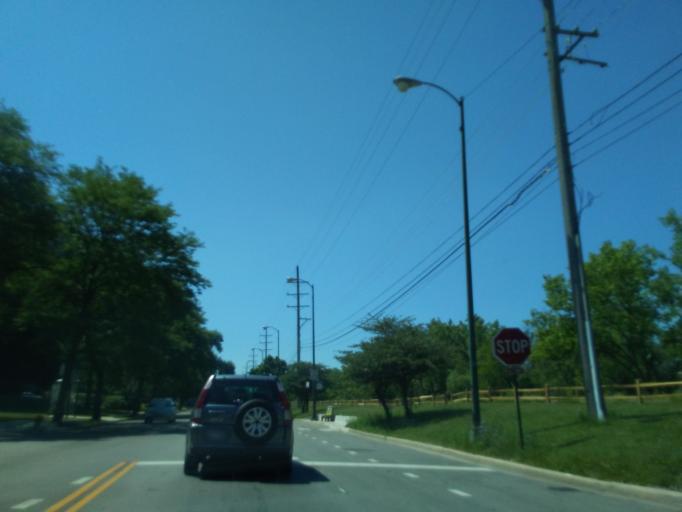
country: US
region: Illinois
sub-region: Cook County
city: Lincolnwood
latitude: 42.0102
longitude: -87.7092
